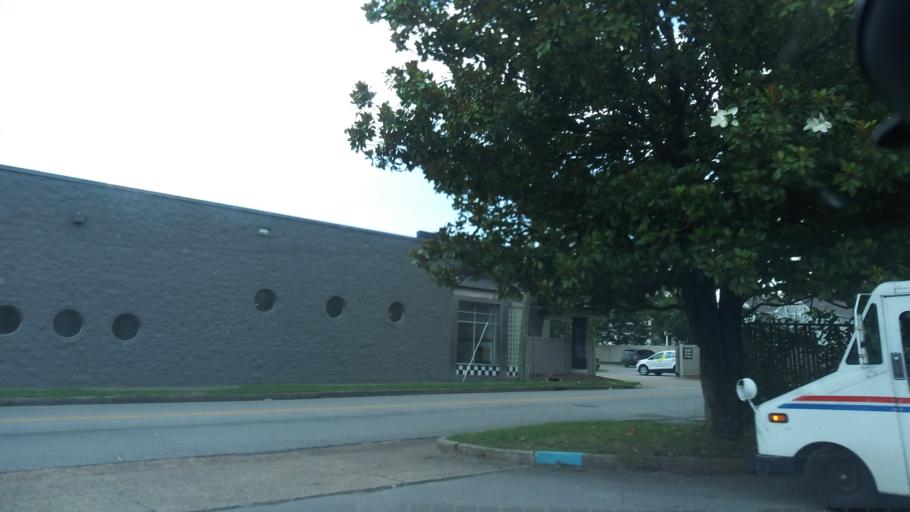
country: US
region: Tennessee
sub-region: Davidson County
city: Nashville
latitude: 36.1549
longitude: -86.8422
